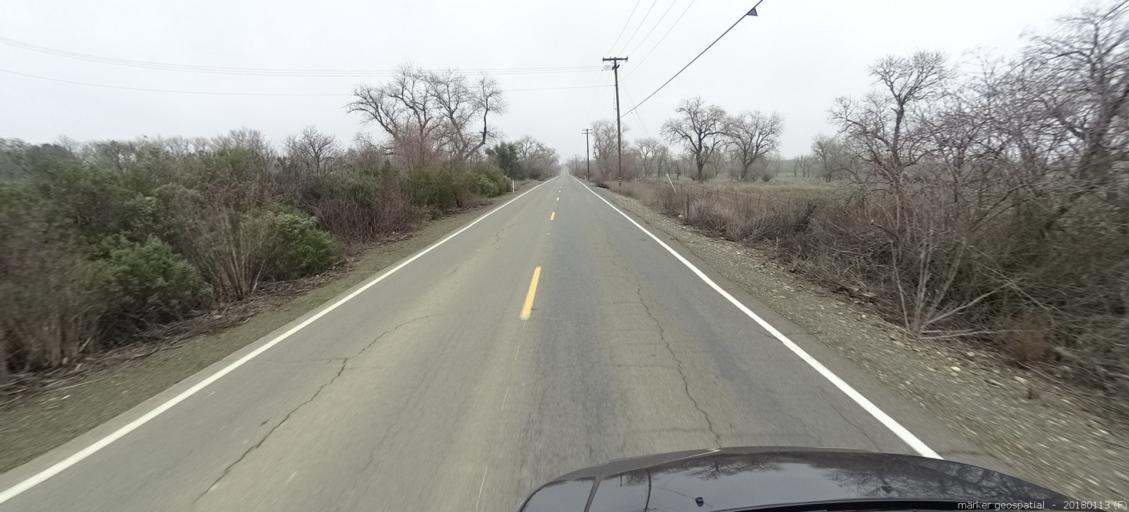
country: US
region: California
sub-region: Sacramento County
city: Gold River
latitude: 38.5929
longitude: -121.2112
